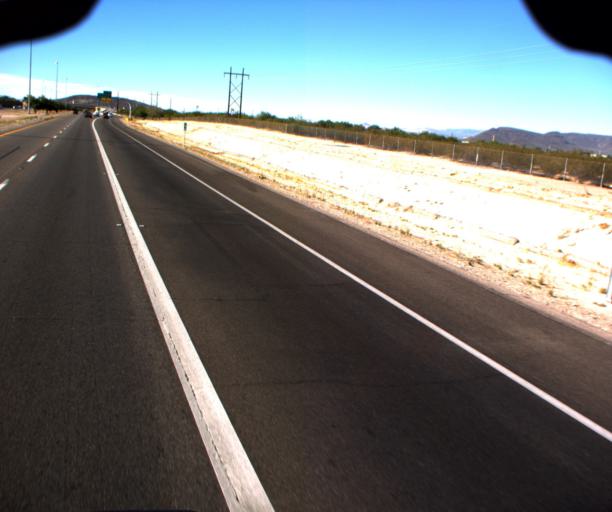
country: US
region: Arizona
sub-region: Pima County
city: Drexel Heights
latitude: 32.1427
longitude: -110.9868
